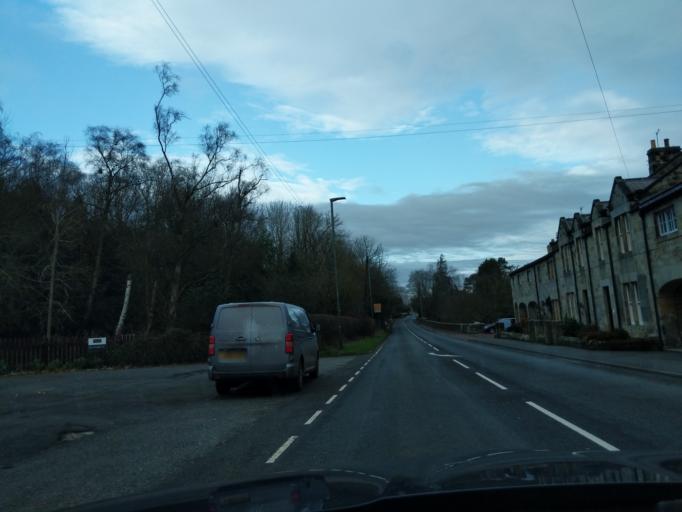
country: GB
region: England
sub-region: Northumberland
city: Meldon
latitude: 55.1027
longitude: -1.8419
